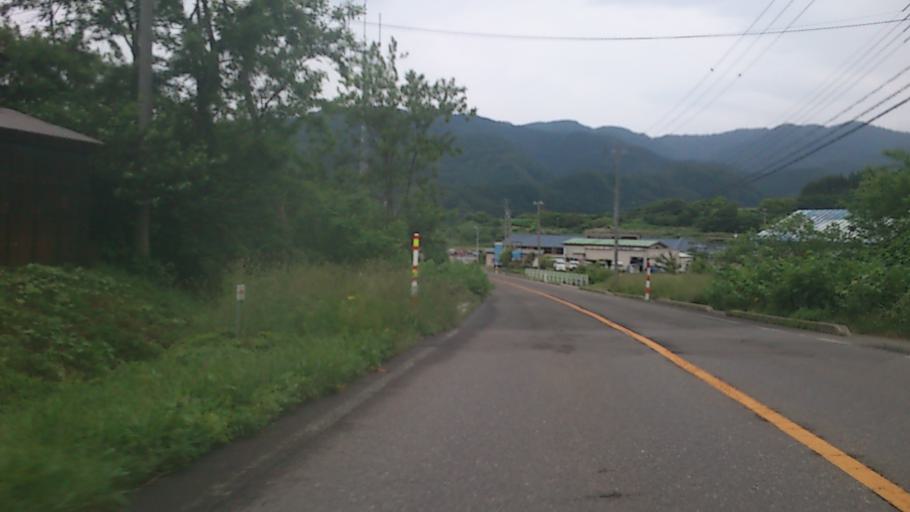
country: JP
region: Akita
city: Noshiromachi
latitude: 40.3707
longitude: 140.0191
